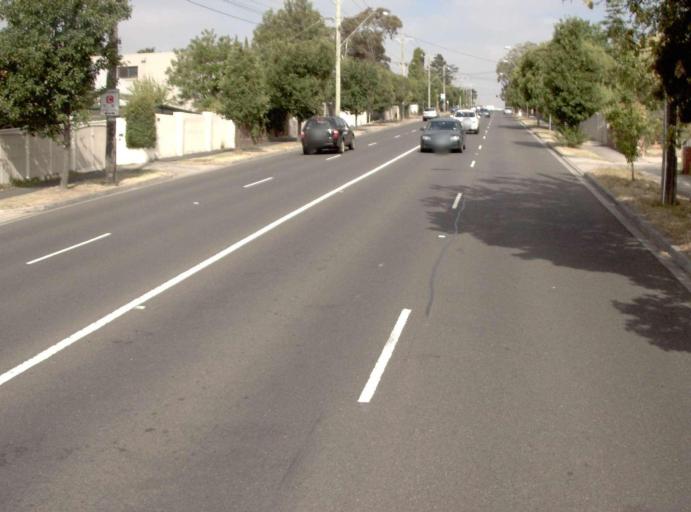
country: AU
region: Victoria
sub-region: Boroondara
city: Camberwell
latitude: -37.8477
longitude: 145.0725
